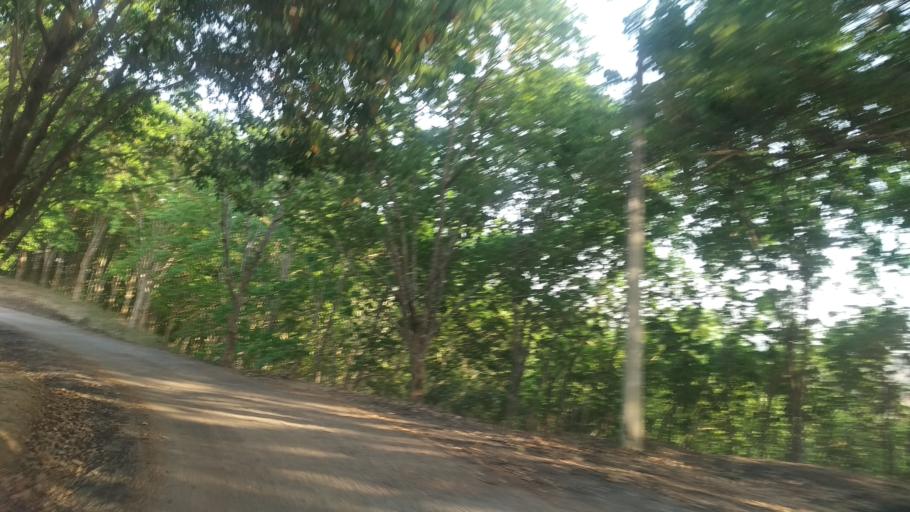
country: IN
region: Tripura
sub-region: West Tripura
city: Sonamura
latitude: 23.4440
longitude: 91.3684
